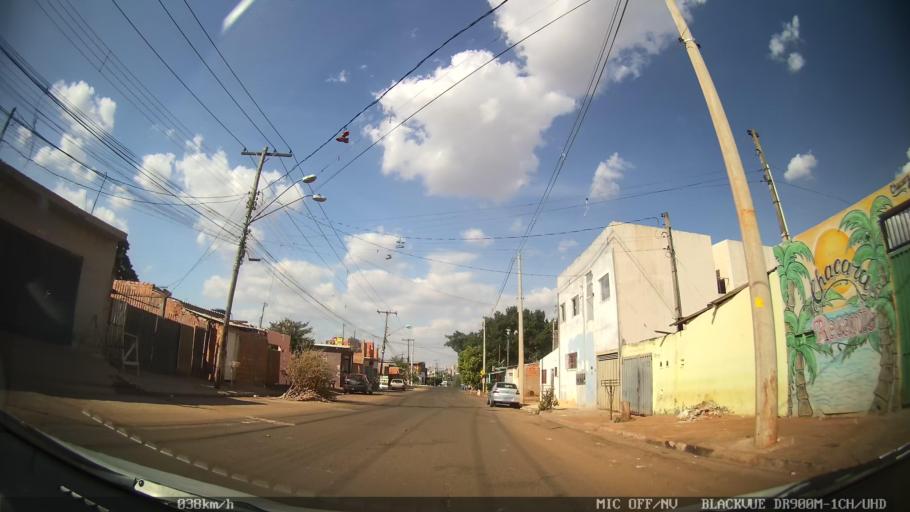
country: BR
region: Sao Paulo
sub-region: Ribeirao Preto
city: Ribeirao Preto
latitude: -21.2049
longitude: -47.8463
